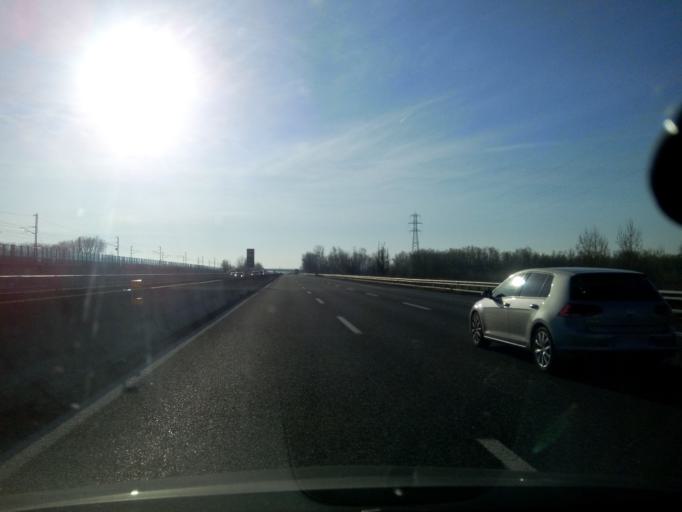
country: IT
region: Emilia-Romagna
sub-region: Provincia di Reggio Emilia
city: Praticello
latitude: 44.8067
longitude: 10.4328
